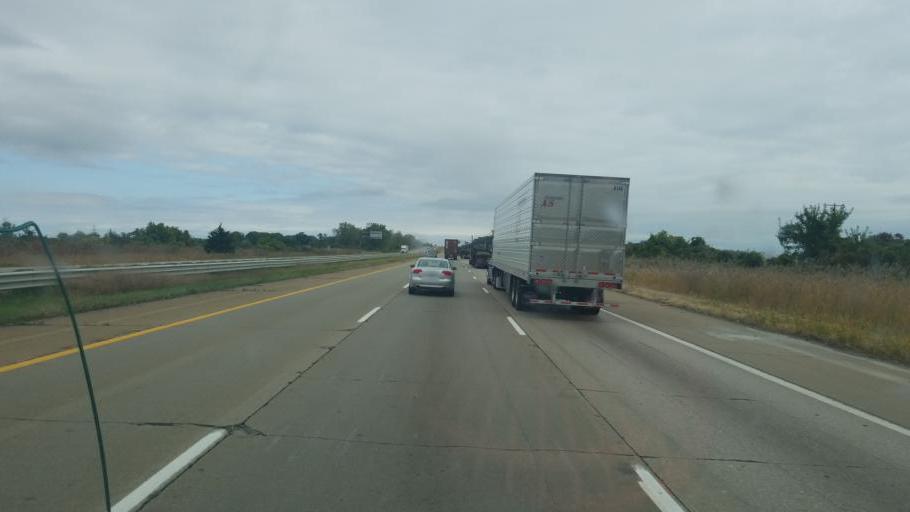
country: US
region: Michigan
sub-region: Monroe County
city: Luna Pier
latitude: 41.7728
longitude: -83.4788
